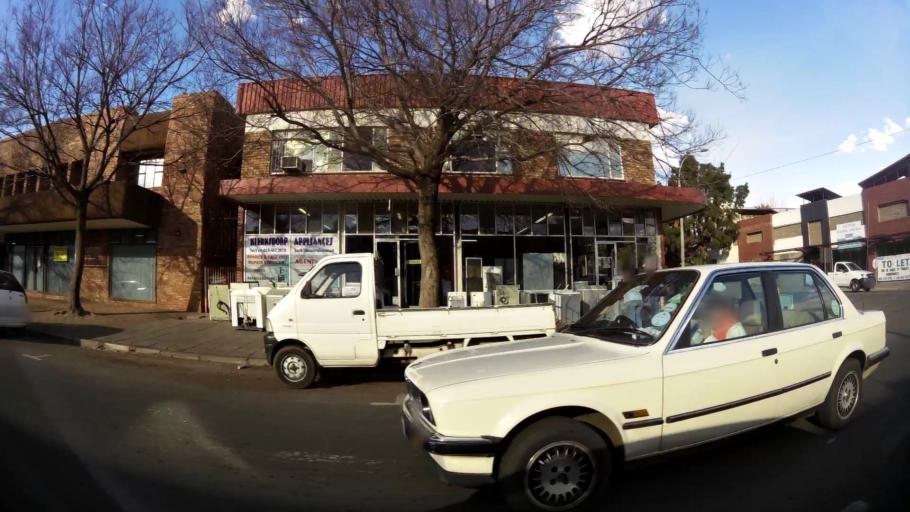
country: ZA
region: North-West
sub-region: Dr Kenneth Kaunda District Municipality
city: Klerksdorp
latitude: -26.8709
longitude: 26.6677
